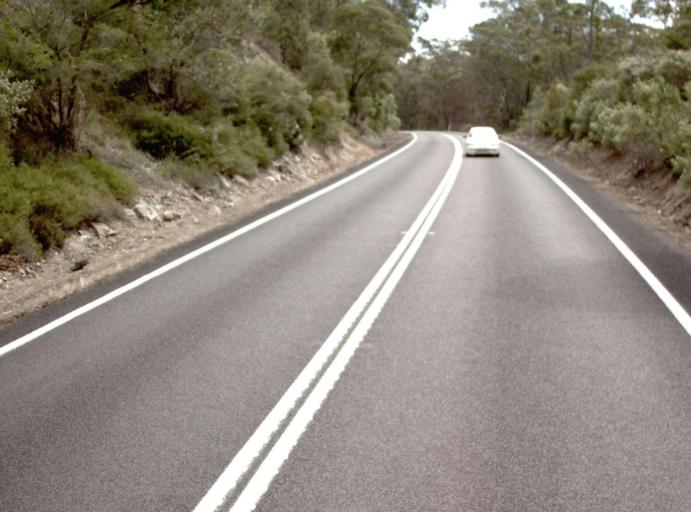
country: AU
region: New South Wales
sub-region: Bega Valley
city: Eden
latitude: -37.4811
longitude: 149.5565
